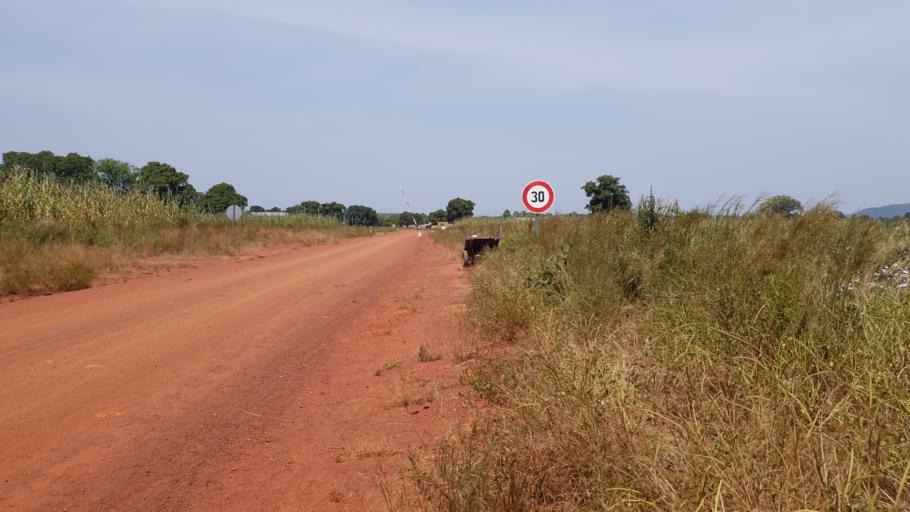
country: ML
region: Sikasso
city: Sikasso
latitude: 11.6064
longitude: -6.3420
